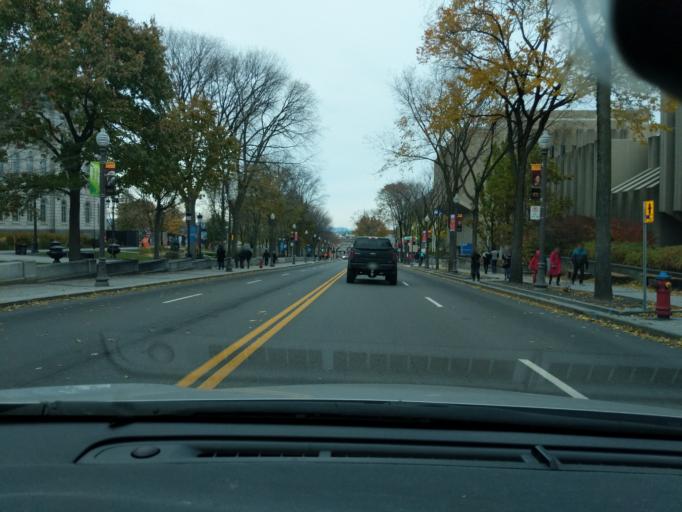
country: CA
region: Quebec
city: Quebec
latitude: 46.8078
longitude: -71.2138
